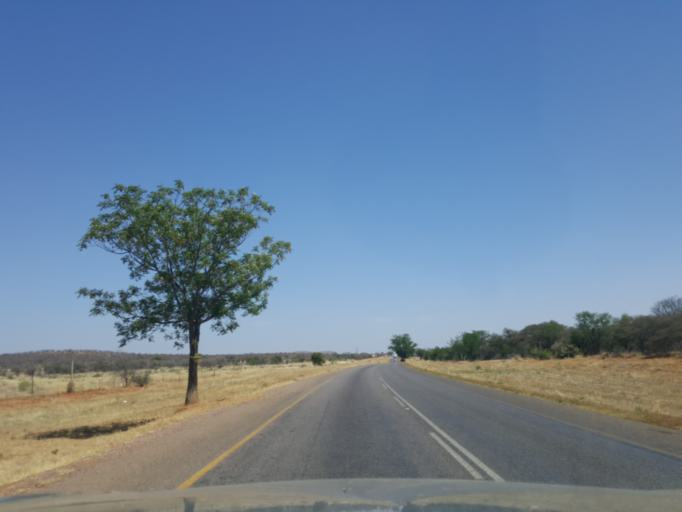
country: BW
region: South East
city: Lobatse
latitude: -25.1597
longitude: 25.6892
